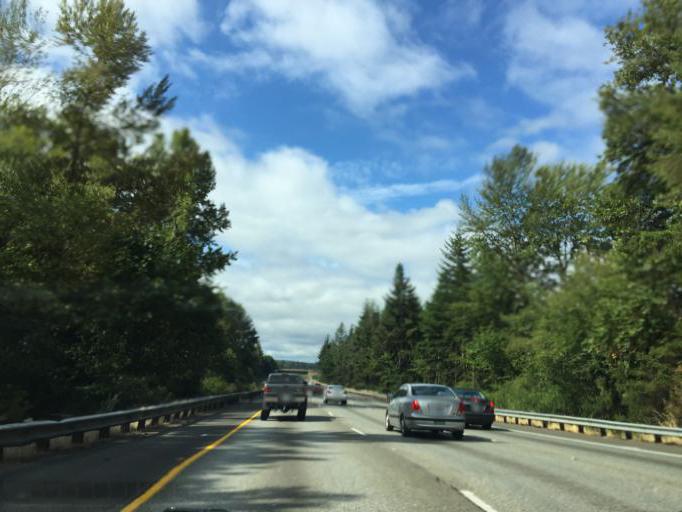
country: US
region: Washington
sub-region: Pierce County
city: DuPont
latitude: 47.0796
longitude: -122.6854
